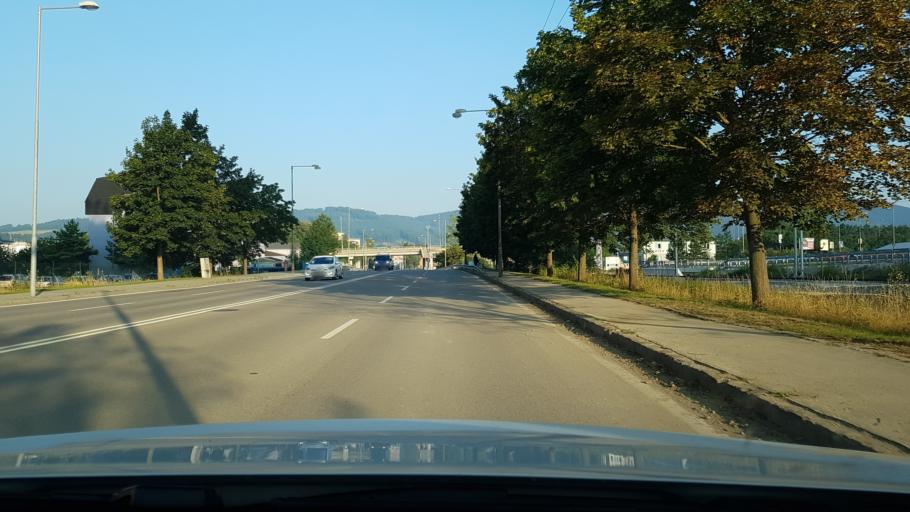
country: SK
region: Trenciansky
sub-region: Okres Povazska Bystrica
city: Povazska Bystrica
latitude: 49.1202
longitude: 18.4416
